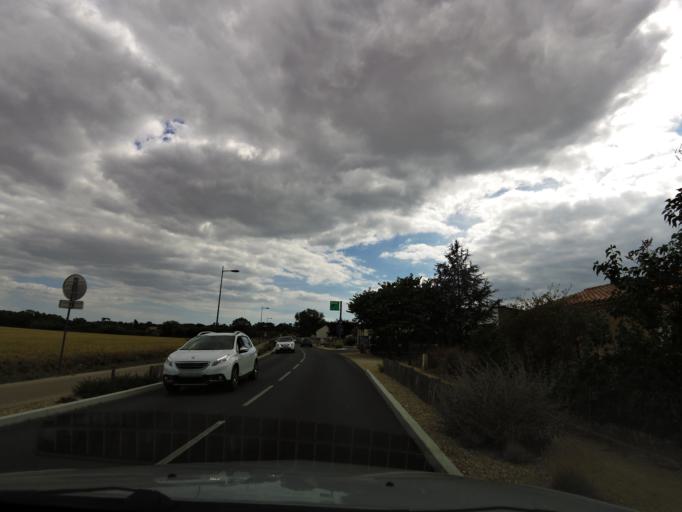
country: FR
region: Pays de la Loire
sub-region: Departement de la Vendee
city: Longeville-sur-Mer
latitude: 46.4152
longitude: -1.4950
